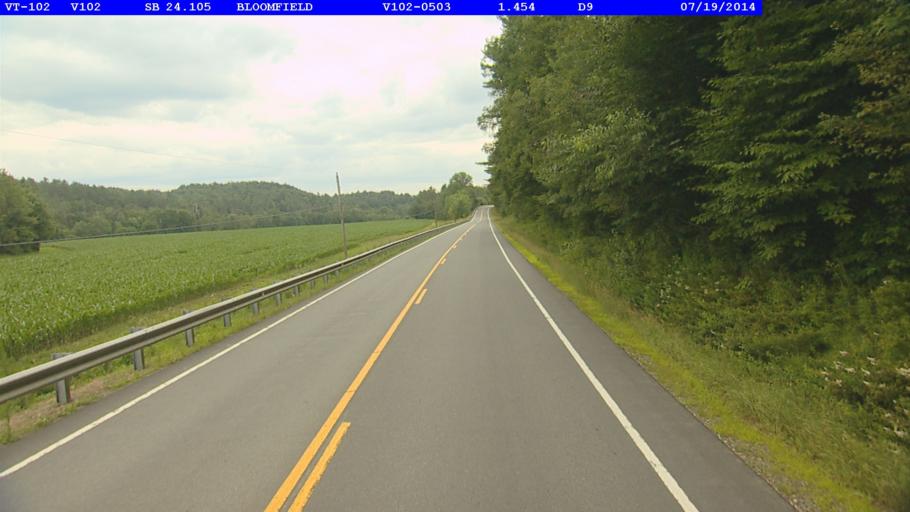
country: US
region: New Hampshire
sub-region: Coos County
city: Stratford
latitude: 44.7628
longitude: -71.6141
